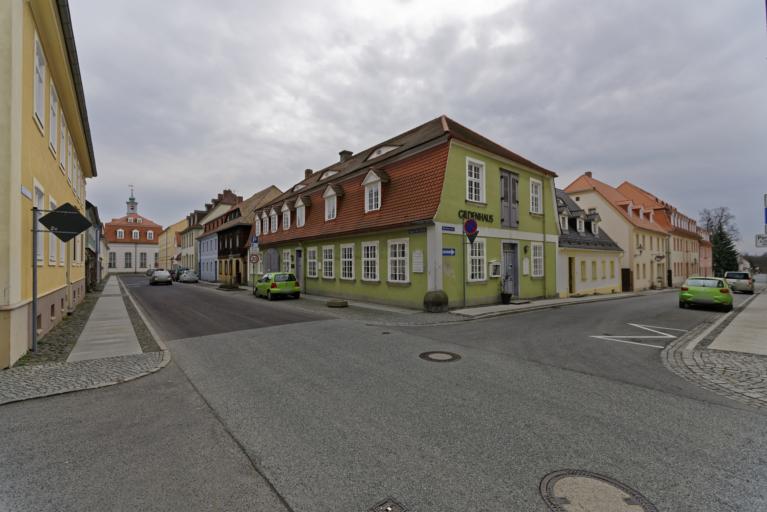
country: DE
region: Saxony
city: Herrnhut
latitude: 51.0172
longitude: 14.7440
